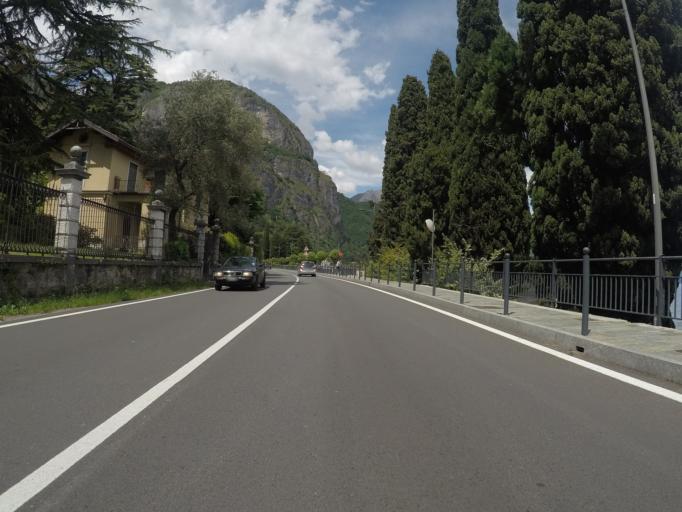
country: IT
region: Lombardy
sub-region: Provincia di Como
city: Griante
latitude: 45.9979
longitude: 9.2382
